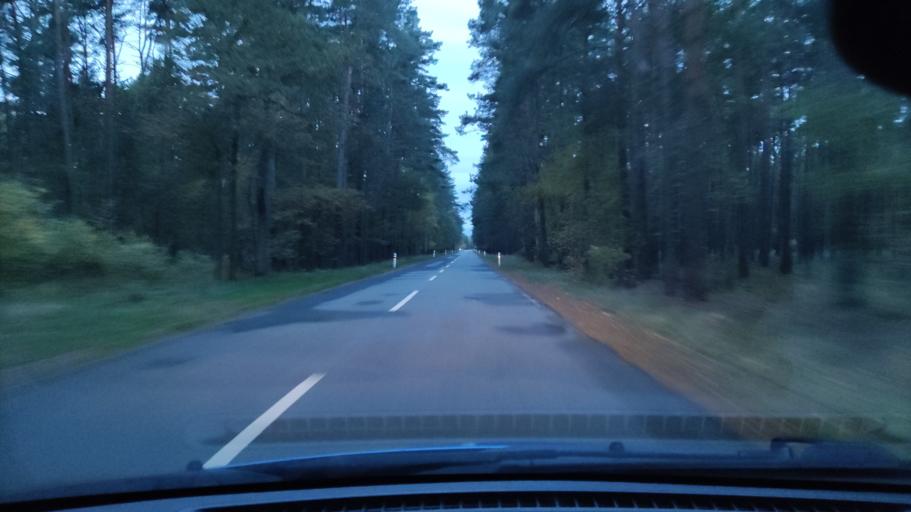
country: DE
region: Lower Saxony
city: Prezelle
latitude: 52.9618
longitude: 11.3744
